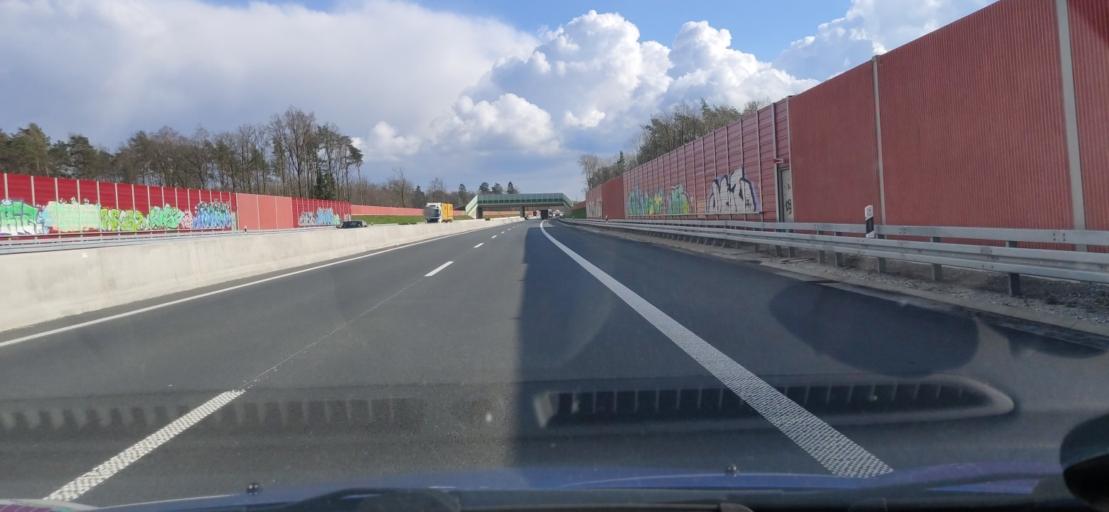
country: DE
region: North Rhine-Westphalia
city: Halle
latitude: 52.0621
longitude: 8.3238
